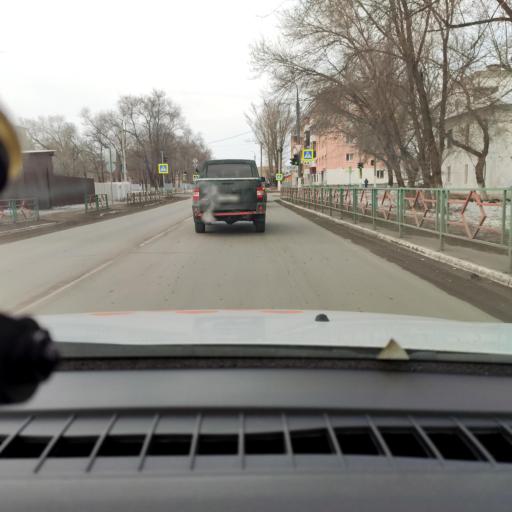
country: RU
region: Samara
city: Chapayevsk
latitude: 52.9533
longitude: 49.6865
